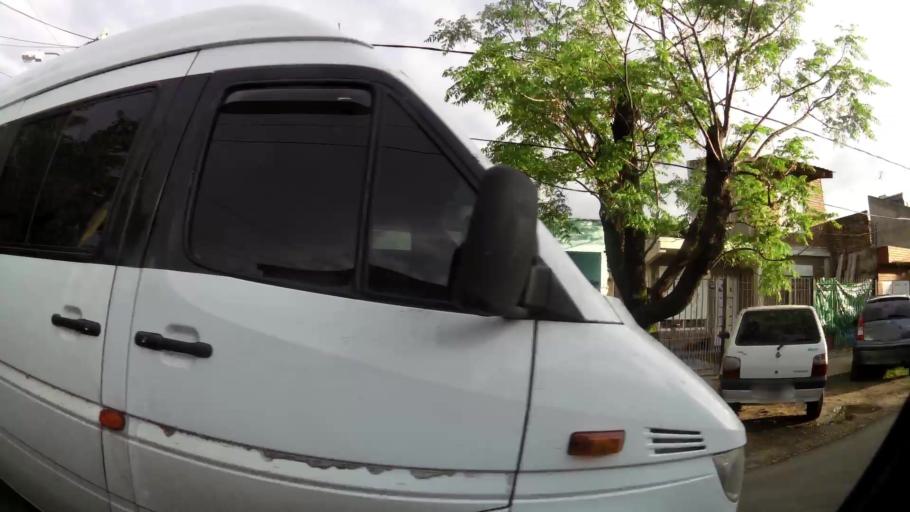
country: AR
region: Buenos Aires
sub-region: Partido de Lomas de Zamora
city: Lomas de Zamora
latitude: -34.7496
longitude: -58.3526
